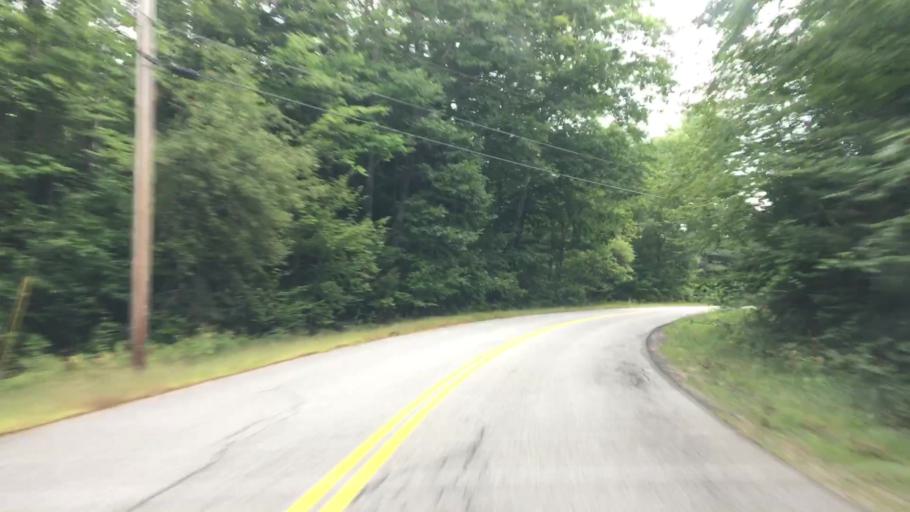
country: US
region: Maine
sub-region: Cumberland County
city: New Gloucester
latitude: 43.9210
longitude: -70.2565
